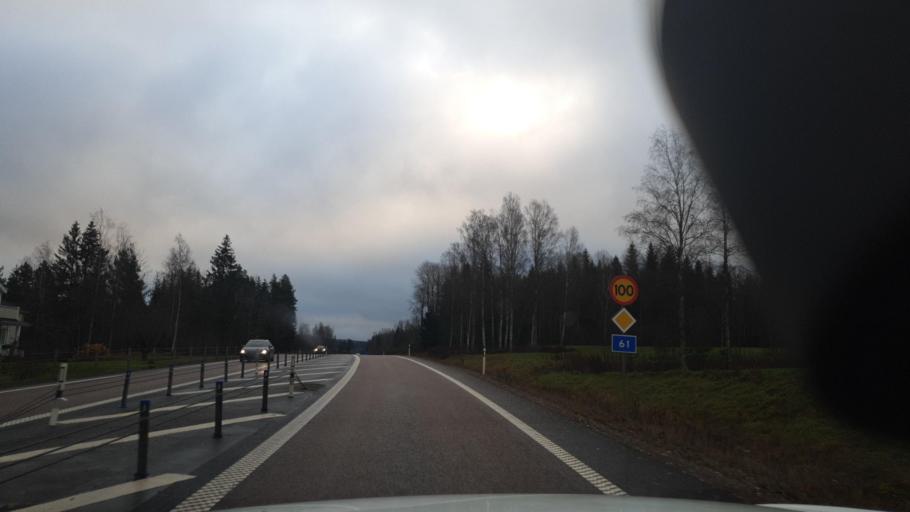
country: SE
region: Vaermland
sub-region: Eda Kommun
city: Amotfors
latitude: 59.7879
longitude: 12.3472
